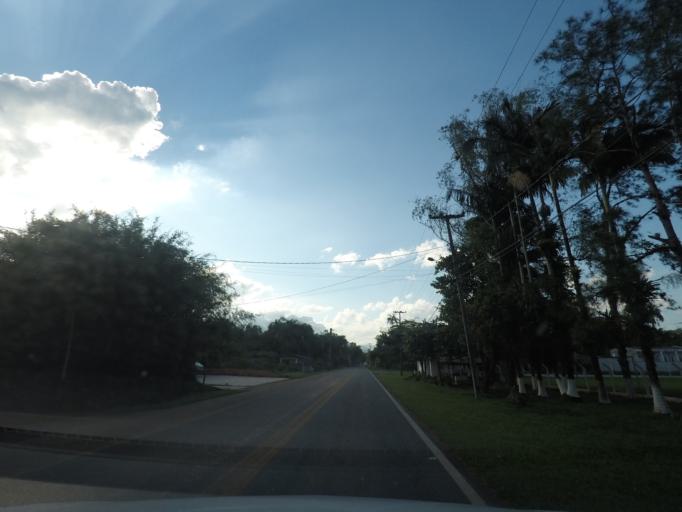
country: BR
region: Parana
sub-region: Antonina
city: Antonina
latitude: -25.4394
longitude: -48.8760
